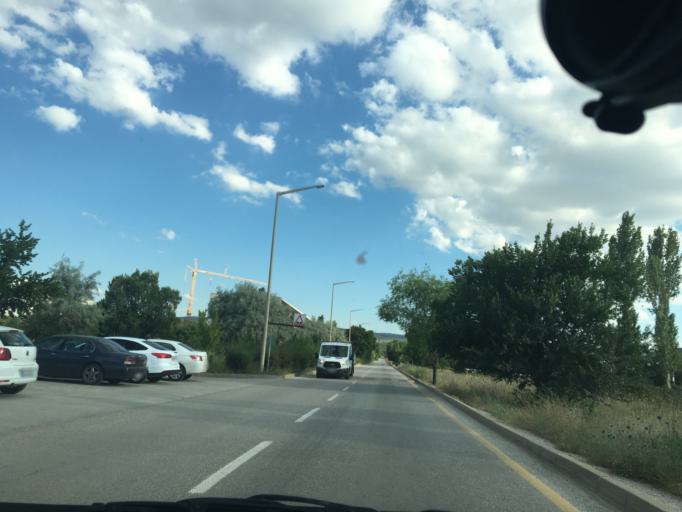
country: TR
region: Ankara
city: Ankara
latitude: 39.8985
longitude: 32.7768
